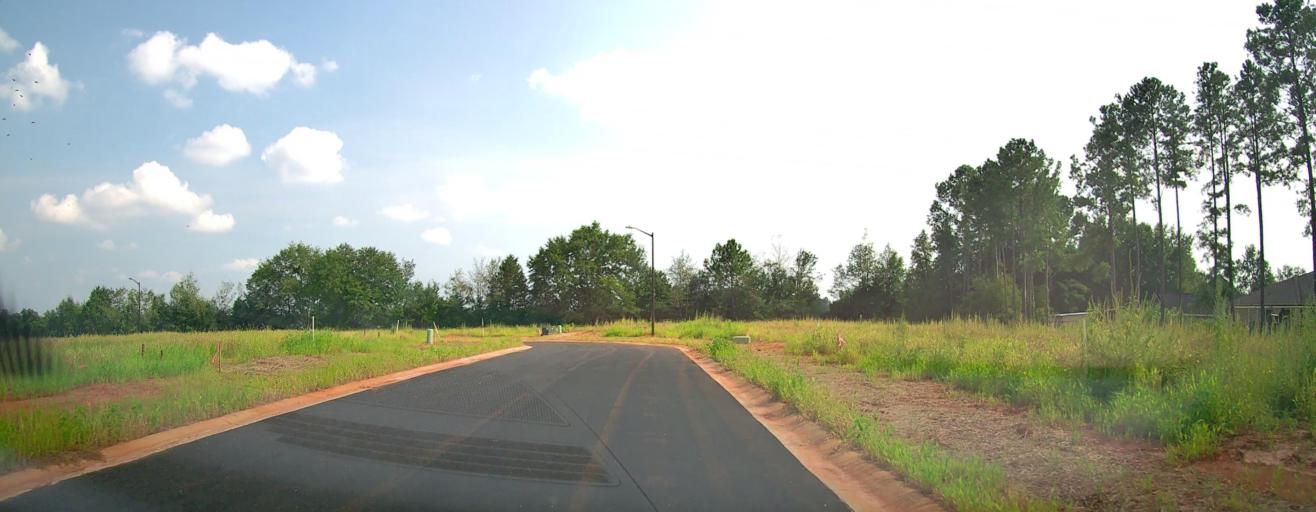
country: US
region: Georgia
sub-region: Houston County
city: Centerville
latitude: 32.6484
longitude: -83.7046
